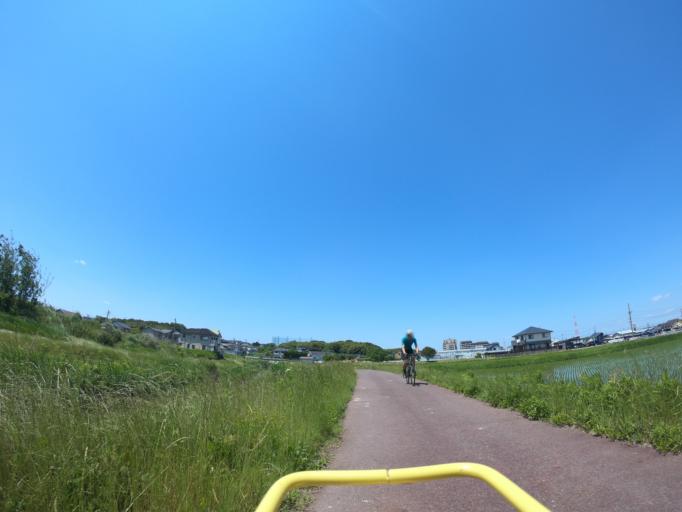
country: JP
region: Aichi
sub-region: Toyota-shi
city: Toyota
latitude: 35.1308
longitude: 137.0584
